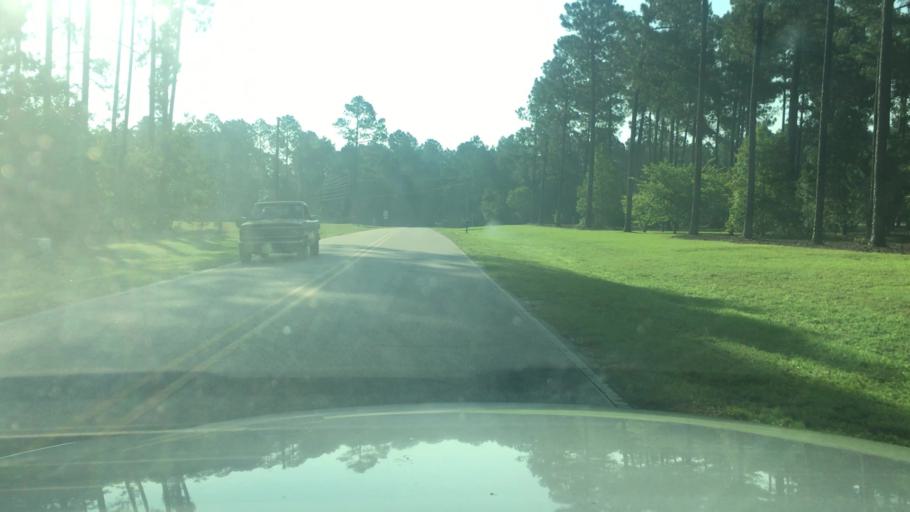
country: US
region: North Carolina
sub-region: Cumberland County
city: Spring Lake
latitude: 35.2066
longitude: -78.8895
